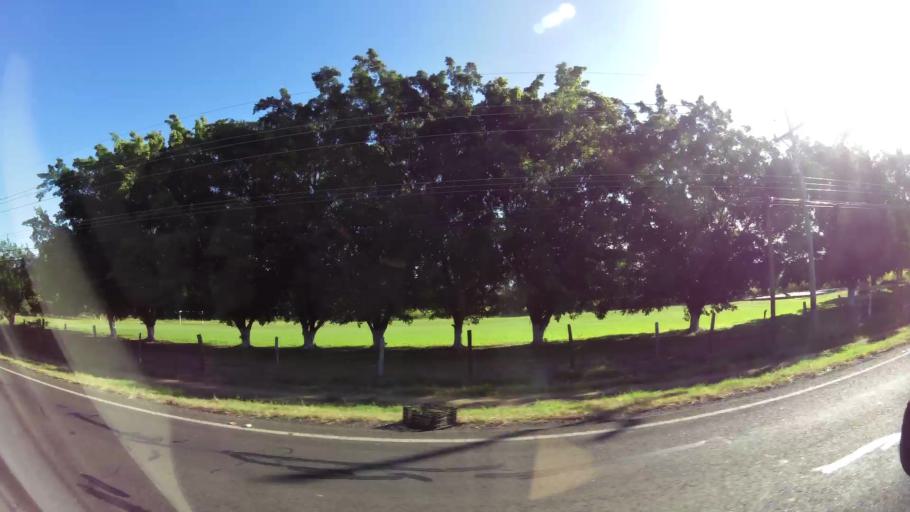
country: CR
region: Guanacaste
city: Belen
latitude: 10.4774
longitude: -85.5641
